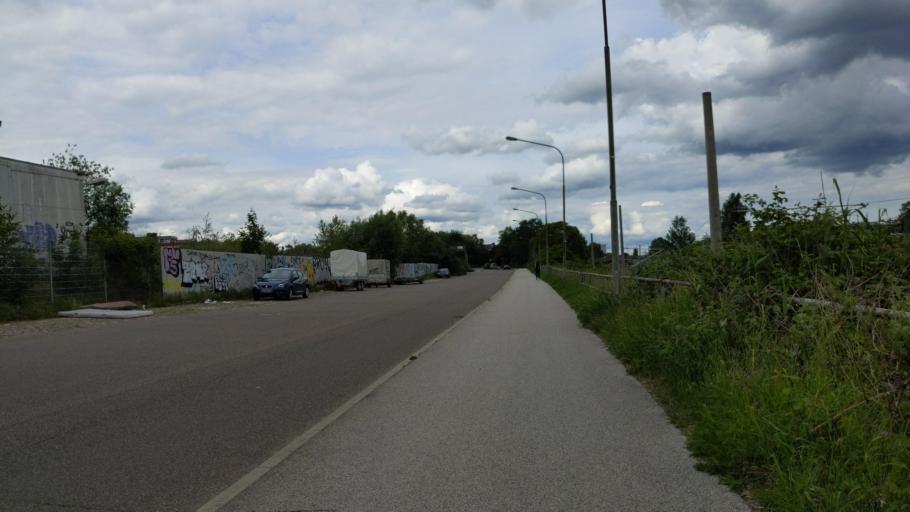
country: DE
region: Schleswig-Holstein
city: Luebeck
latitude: 53.8769
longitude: 10.6806
